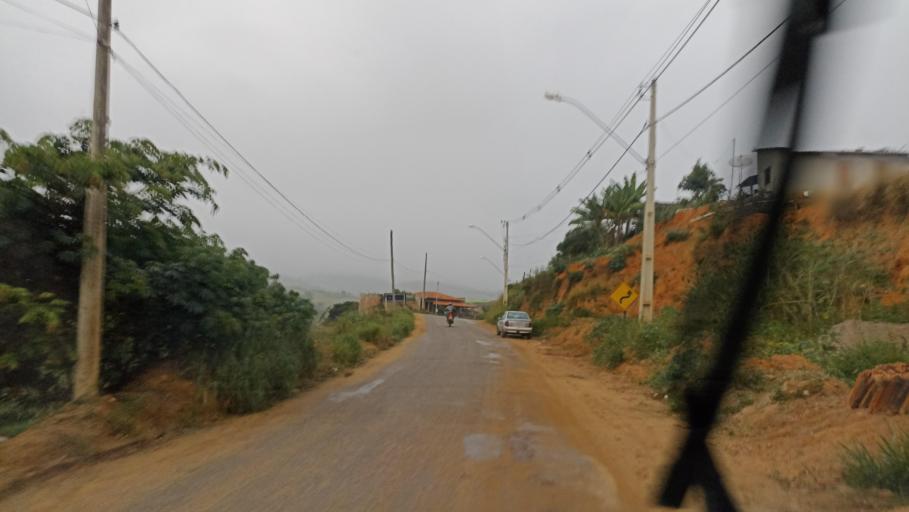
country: BR
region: Bahia
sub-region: Itanhem
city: Itanhem
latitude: -16.7348
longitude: -40.4277
